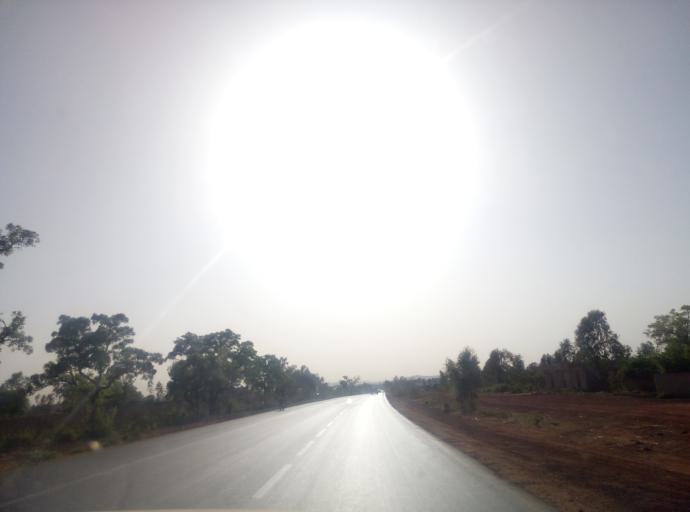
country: ML
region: Bamako
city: Bamako
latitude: 12.5766
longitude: -7.7940
